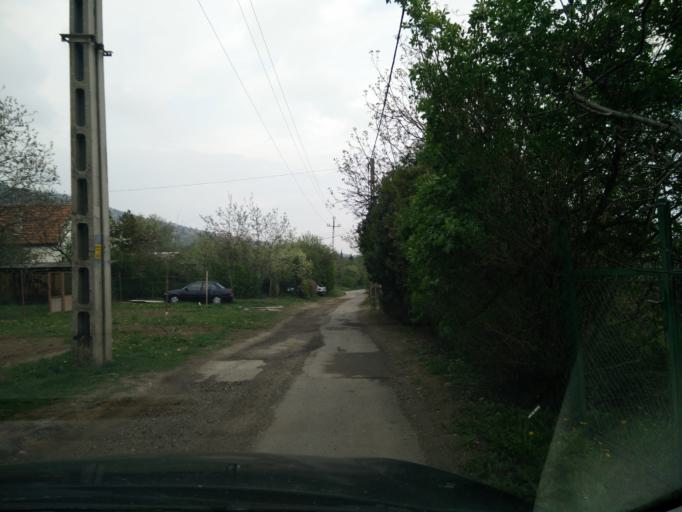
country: HU
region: Pest
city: Budaors
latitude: 47.4704
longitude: 18.9467
